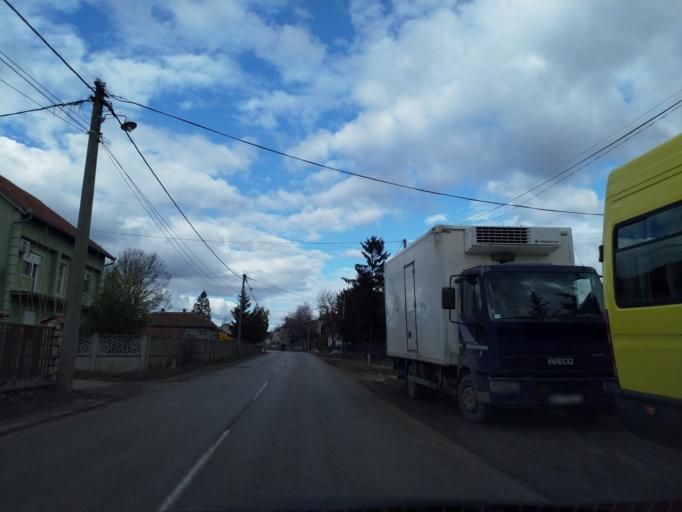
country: RS
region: Central Serbia
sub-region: Belgrade
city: Grocka
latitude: 44.6070
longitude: 20.7252
